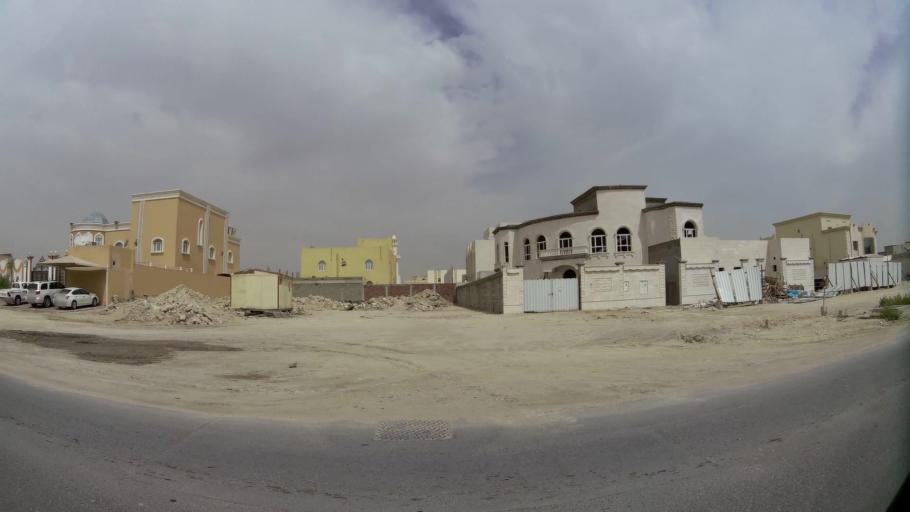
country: QA
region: Al Wakrah
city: Al Wukayr
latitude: 25.2059
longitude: 51.4656
